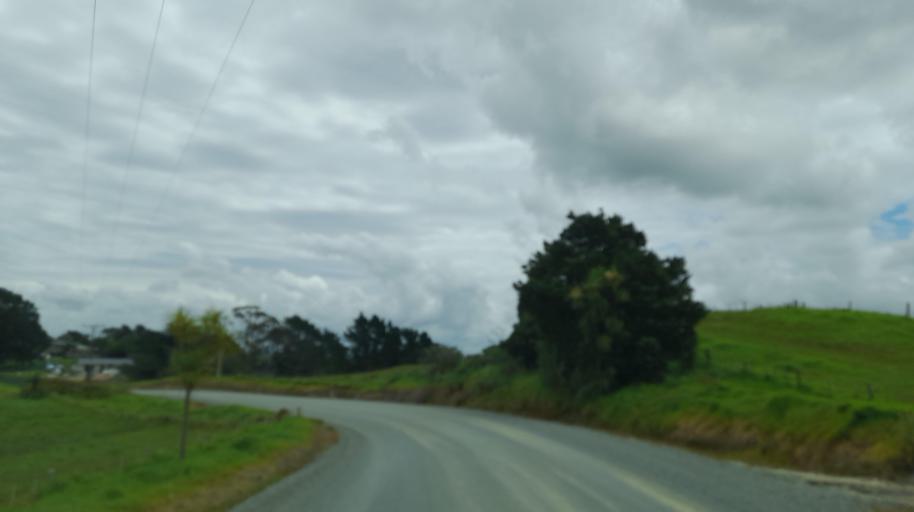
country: NZ
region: Auckland
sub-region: Auckland
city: Wellsford
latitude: -36.2485
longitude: 174.4185
